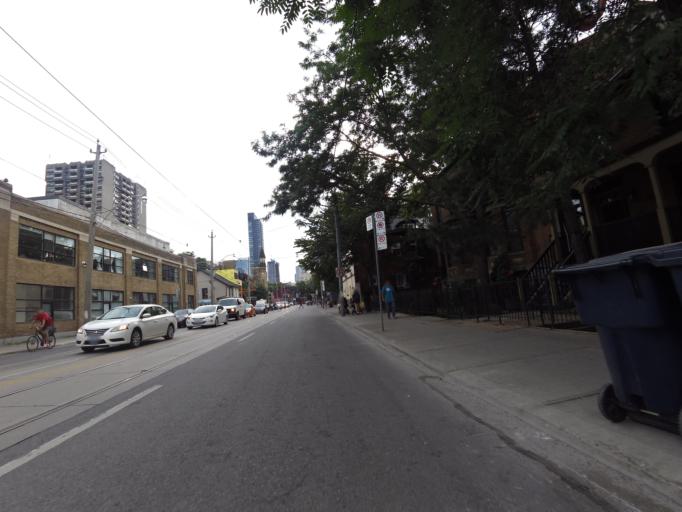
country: CA
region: Ontario
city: Toronto
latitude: 43.6589
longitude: -79.3688
